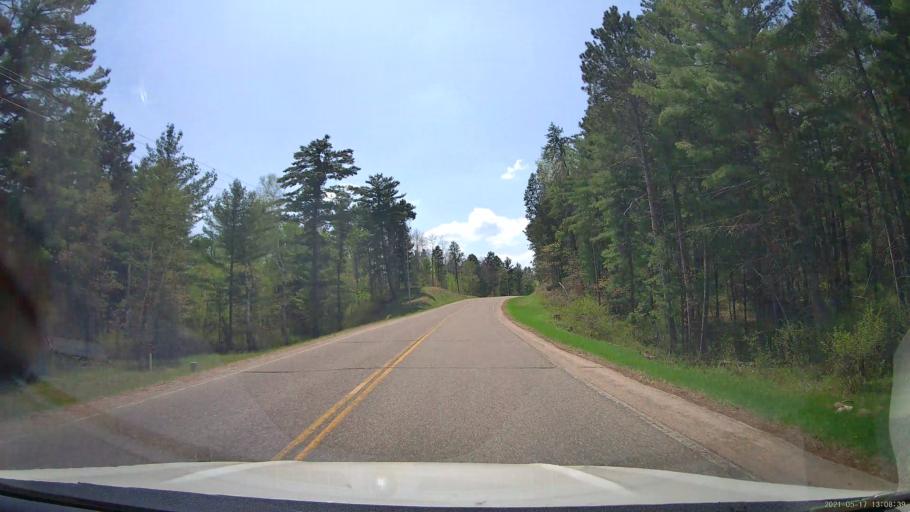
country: US
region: Minnesota
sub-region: Hubbard County
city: Park Rapids
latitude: 47.0349
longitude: -94.9184
